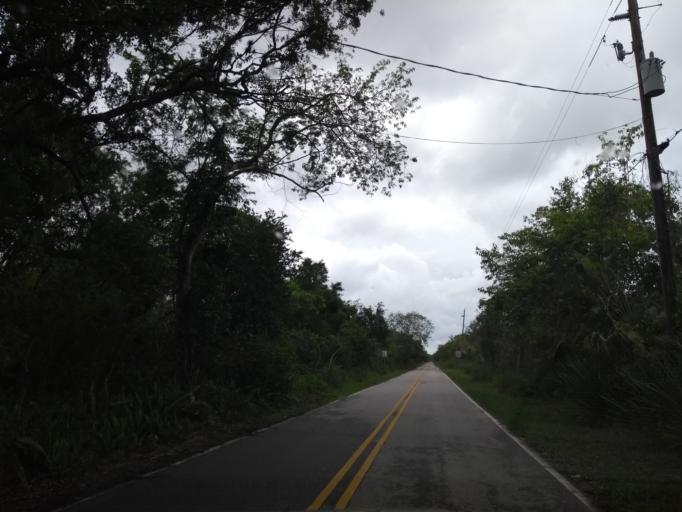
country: US
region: Florida
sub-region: Miami-Dade County
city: The Hammocks
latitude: 25.7607
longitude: -80.9229
